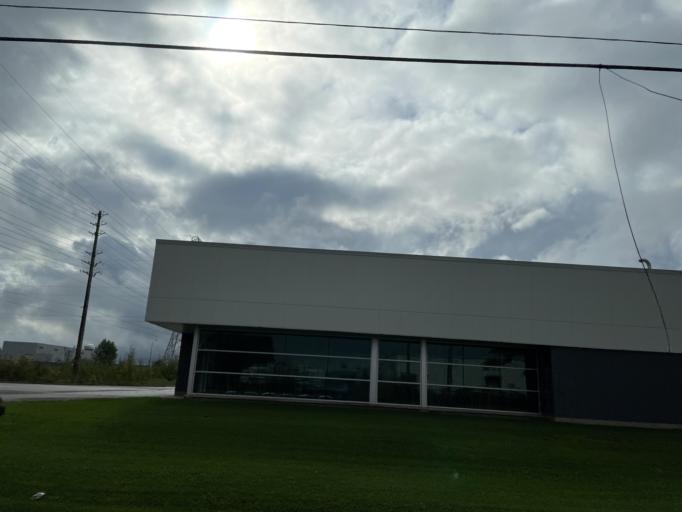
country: CA
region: Ontario
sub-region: Wellington County
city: Guelph
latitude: 43.5484
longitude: -80.2921
